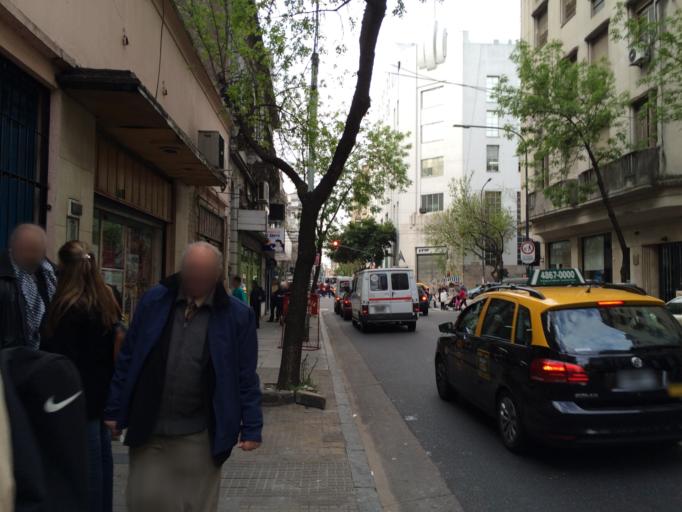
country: AR
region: Buenos Aires F.D.
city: Buenos Aires
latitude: -34.6103
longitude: -58.4018
